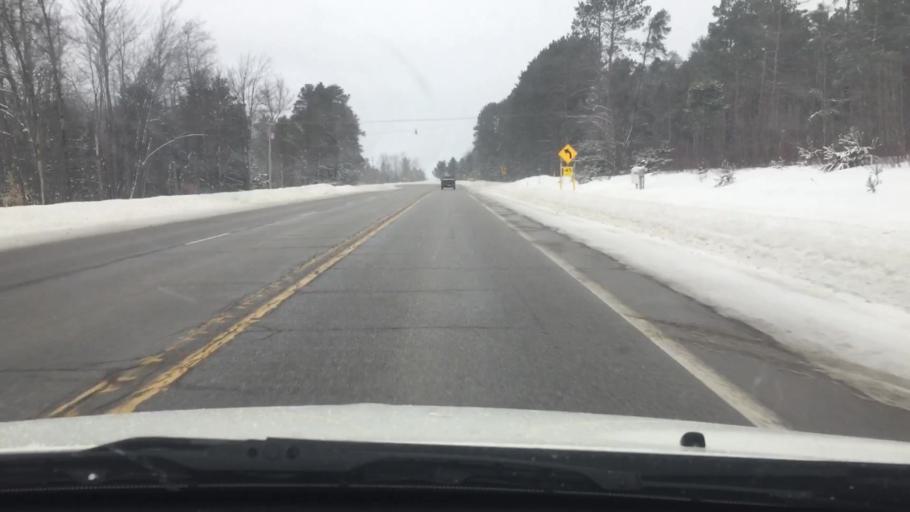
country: US
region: Michigan
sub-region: Otsego County
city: Gaylord
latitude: 45.0565
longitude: -84.7759
